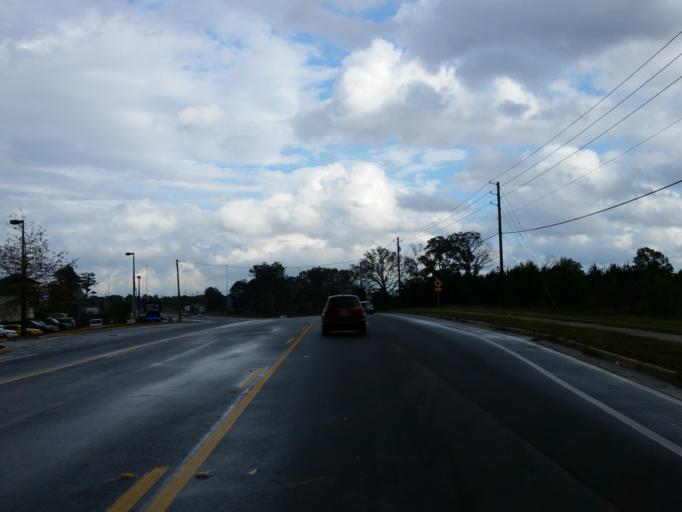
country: US
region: Georgia
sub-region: Henry County
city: Stockbridge
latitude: 33.4818
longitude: -84.2248
